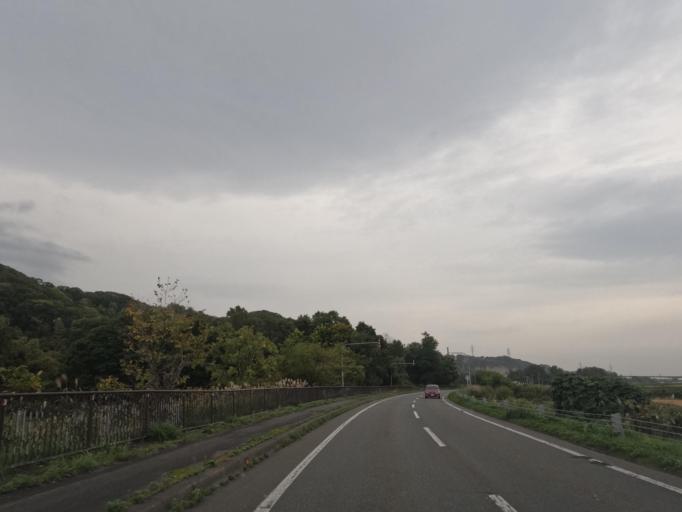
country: JP
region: Hokkaido
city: Date
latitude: 42.5155
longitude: 140.8641
